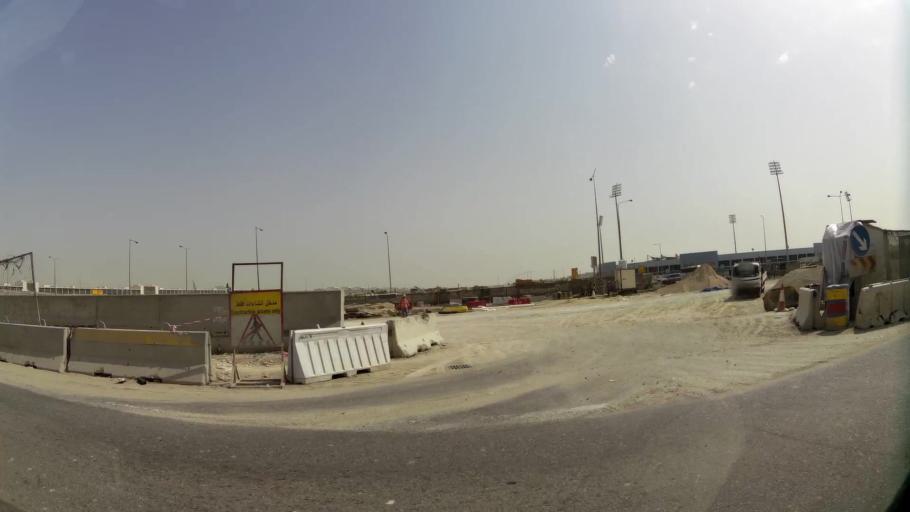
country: QA
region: Al Wakrah
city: Al Wukayr
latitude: 25.1896
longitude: 51.4570
